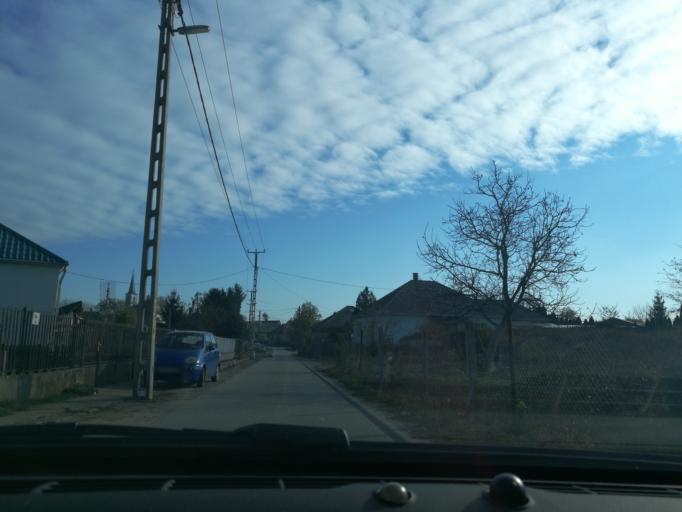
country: HU
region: Szabolcs-Szatmar-Bereg
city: Nyirpazony
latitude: 47.9592
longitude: 21.8010
